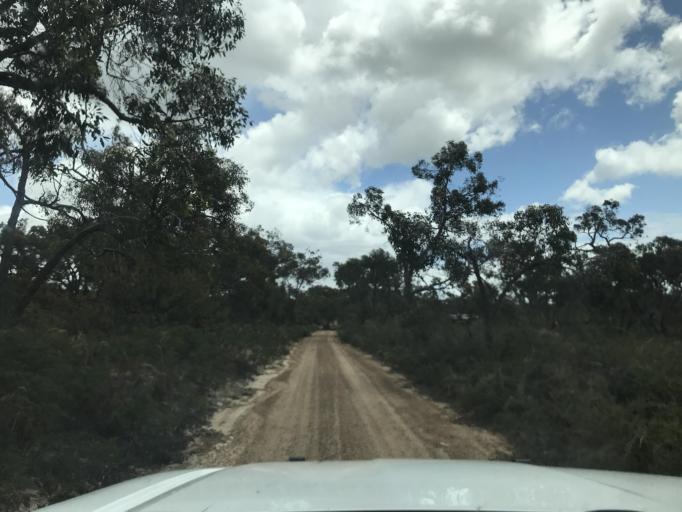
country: AU
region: South Australia
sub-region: Wattle Range
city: Penola
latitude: -37.0890
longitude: 141.3355
